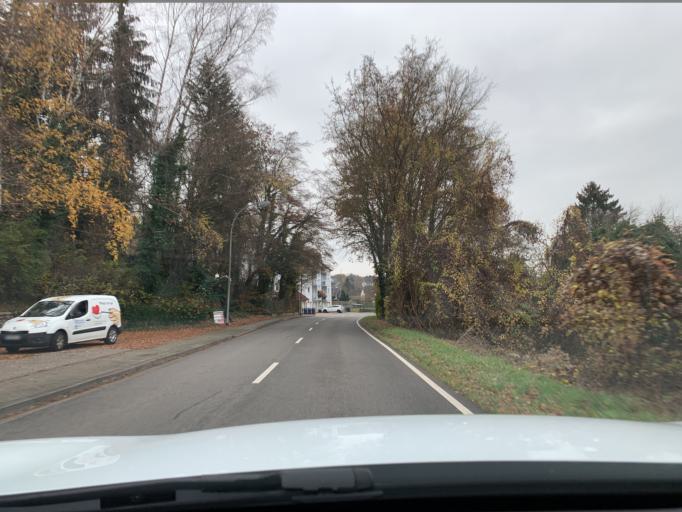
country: DE
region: Saarland
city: Kleinblittersdorf
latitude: 49.1900
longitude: 7.0381
